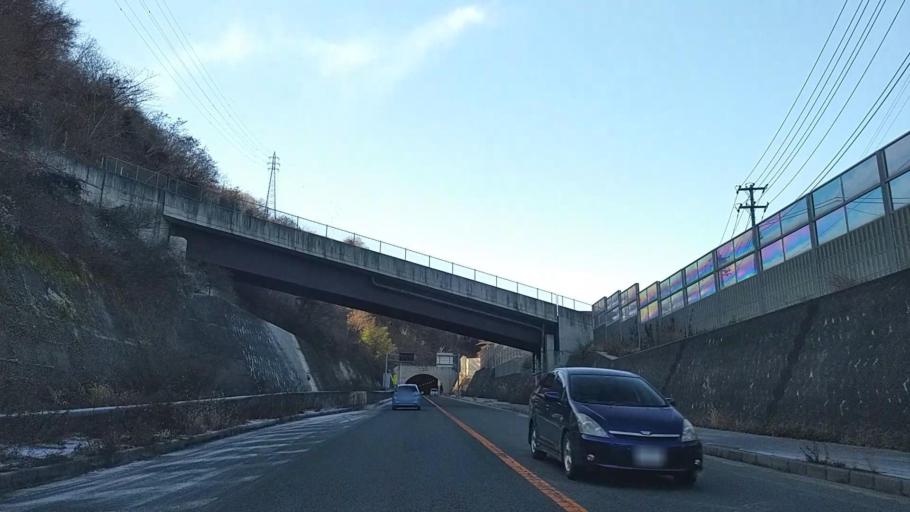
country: JP
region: Yamanashi
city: Otsuki
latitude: 35.6122
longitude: 138.9536
